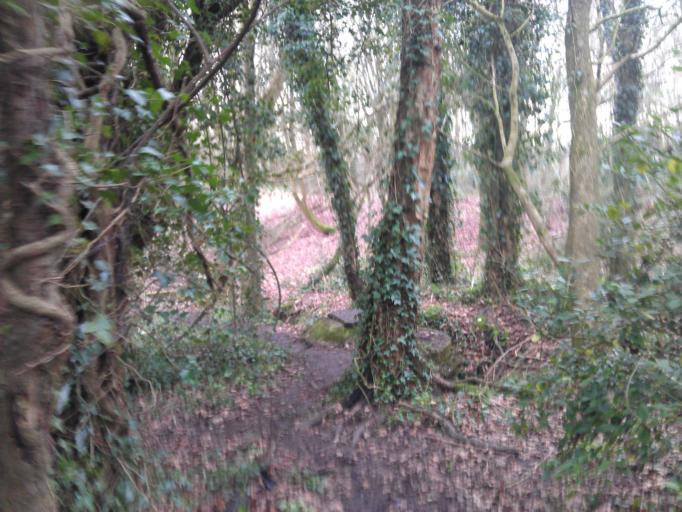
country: GB
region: England
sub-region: Essex
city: Wivenhoe
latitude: 51.8648
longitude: 0.9529
